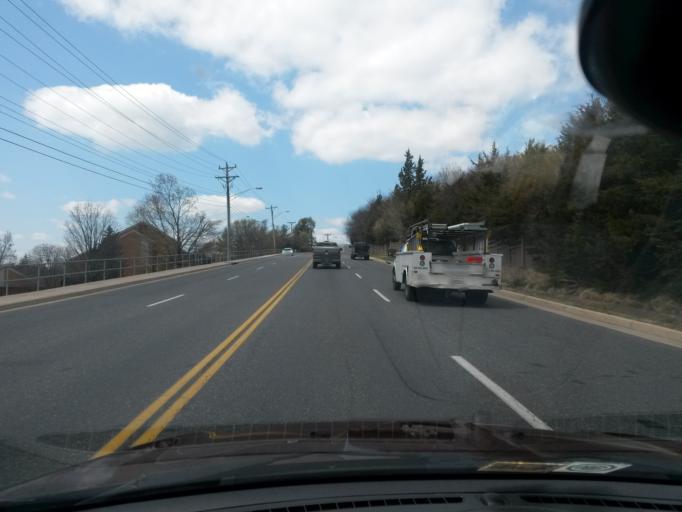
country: US
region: Virginia
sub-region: City of Harrisonburg
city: Harrisonburg
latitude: 38.4388
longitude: -78.8665
